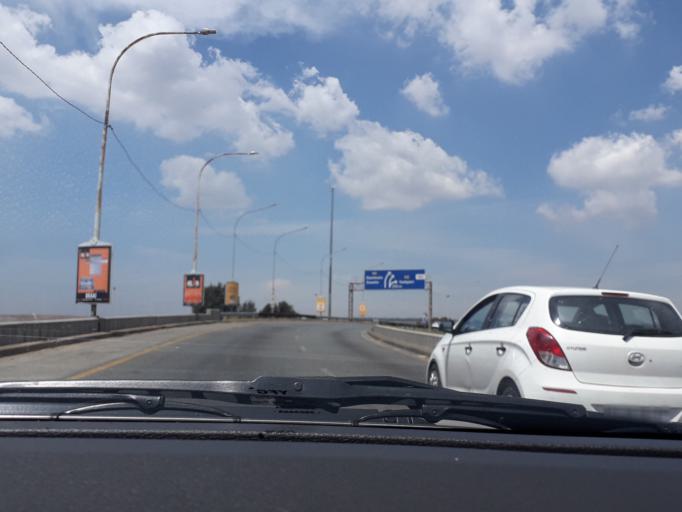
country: ZA
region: Gauteng
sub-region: City of Johannesburg Metropolitan Municipality
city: Johannesburg
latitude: -26.2105
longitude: 28.0308
